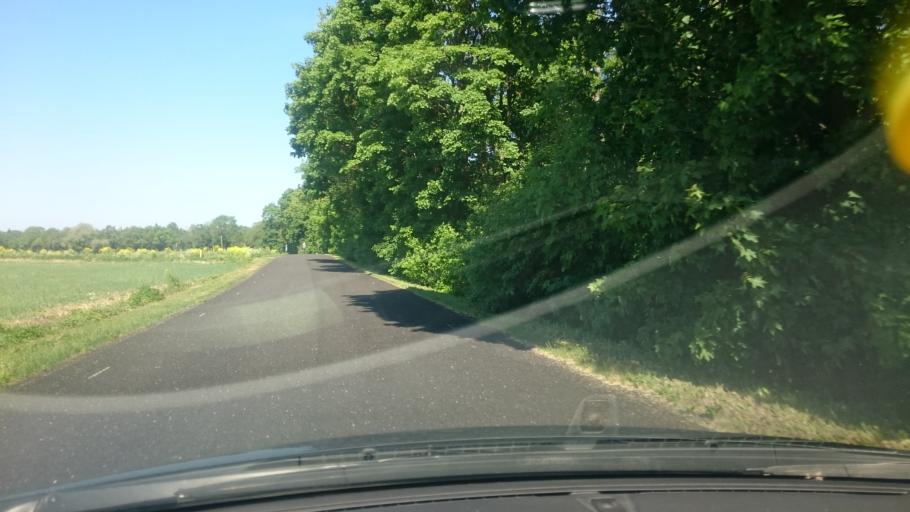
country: EE
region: Harju
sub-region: Rae vald
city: Vaida
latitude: 59.2231
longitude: 24.9663
